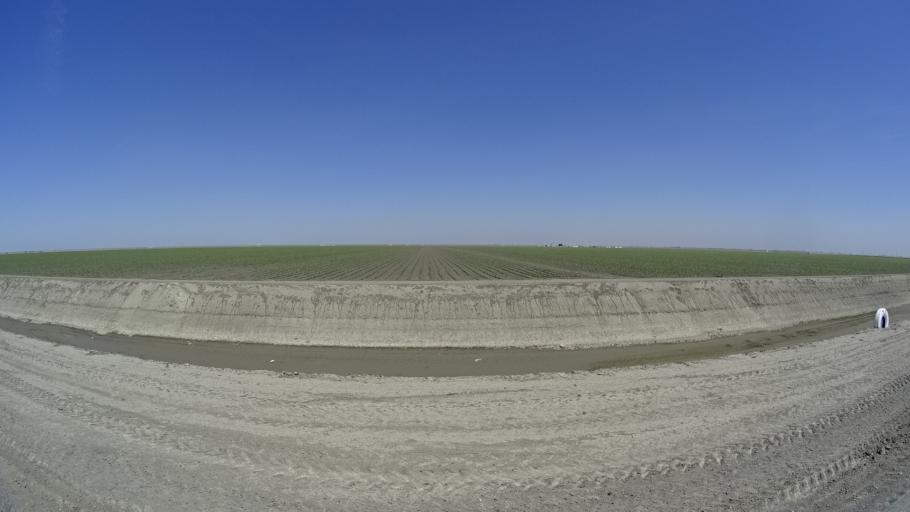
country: US
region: California
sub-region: Kings County
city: Corcoran
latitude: 36.0214
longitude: -119.6526
